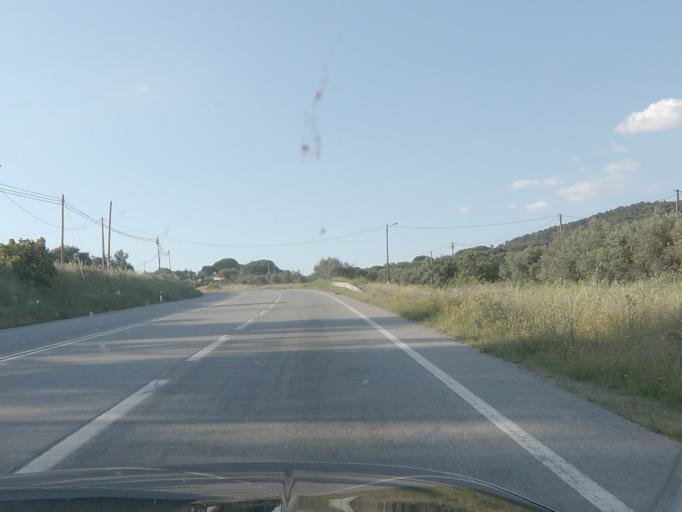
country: PT
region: Portalegre
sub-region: Portalegre
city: Portalegre
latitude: 39.3014
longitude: -7.4393
